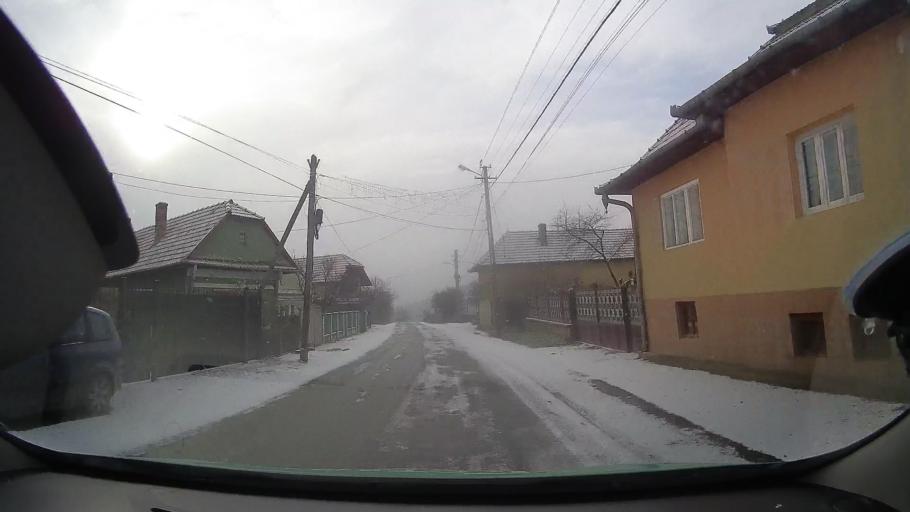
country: RO
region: Alba
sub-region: Comuna Rimetea
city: Rimetea
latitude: 46.4181
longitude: 23.5589
